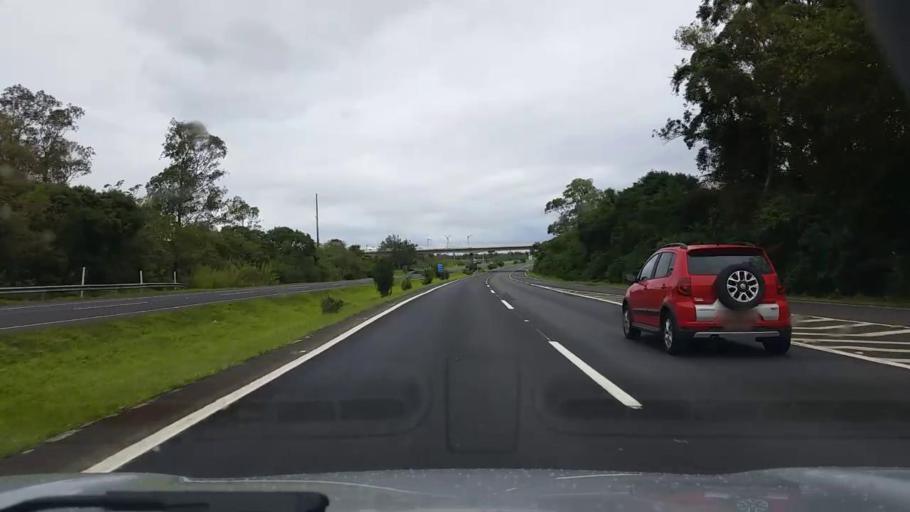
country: BR
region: Rio Grande do Sul
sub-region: Osorio
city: Osorio
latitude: -29.8926
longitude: -50.2825
